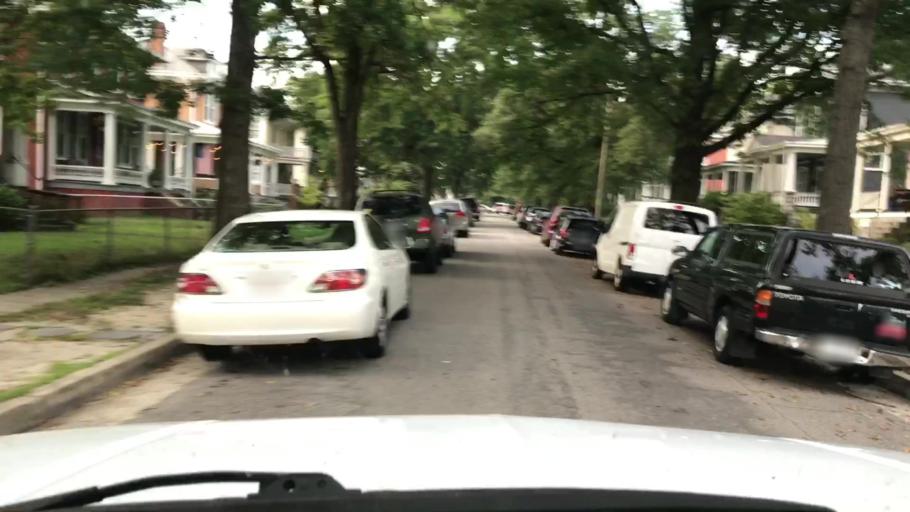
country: US
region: Virginia
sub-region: City of Richmond
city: Richmond
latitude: 37.5705
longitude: -77.4410
